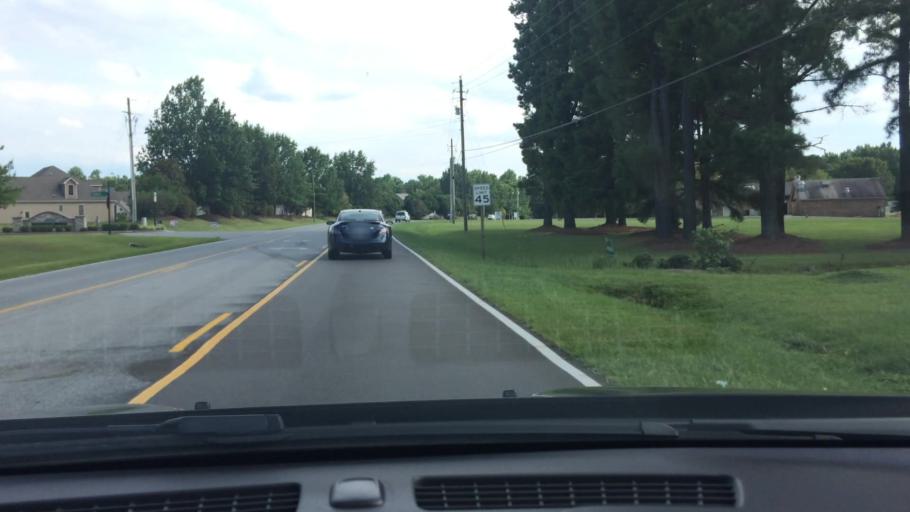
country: US
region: North Carolina
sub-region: Pitt County
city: Windsor
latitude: 35.5468
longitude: -77.3837
